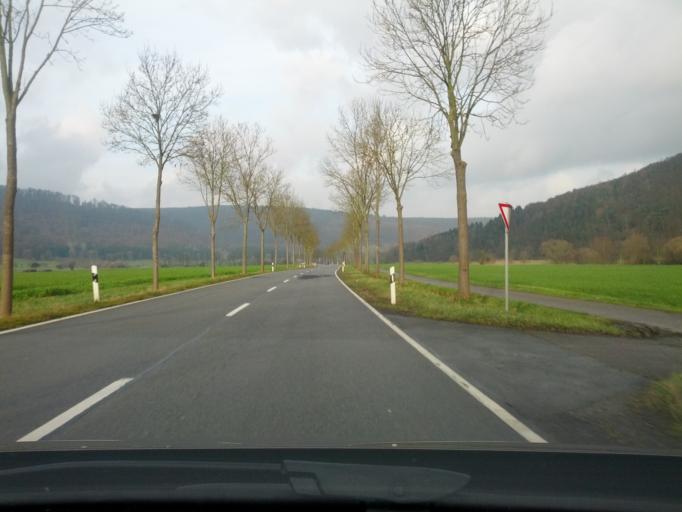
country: DE
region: Lower Saxony
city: Buhren
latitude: 51.5039
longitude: 9.5980
